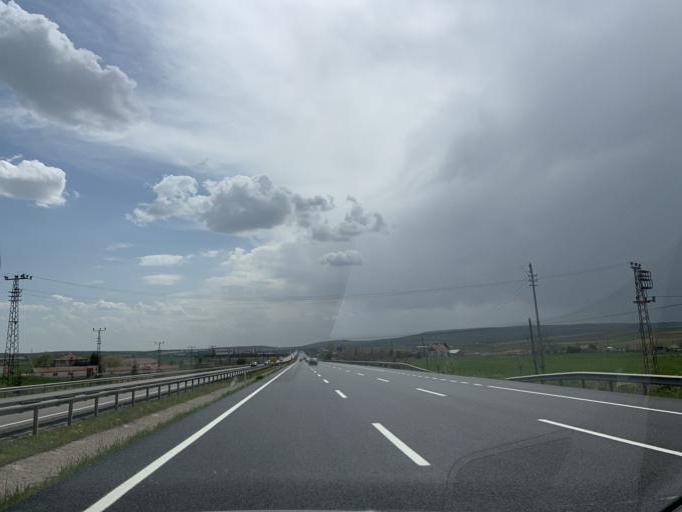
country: TR
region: Ankara
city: Polatli
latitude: 39.6666
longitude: 32.2272
